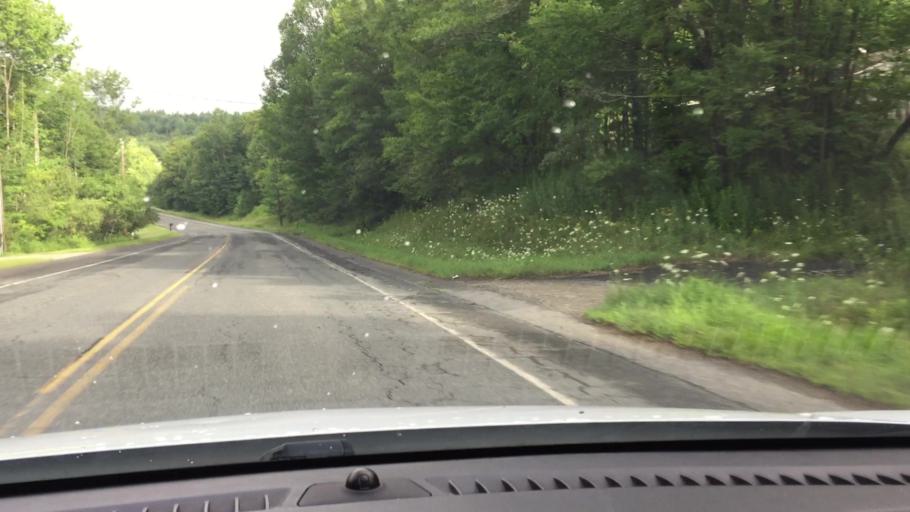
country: US
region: Massachusetts
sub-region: Berkshire County
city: Hinsdale
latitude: 42.4323
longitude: -73.0183
